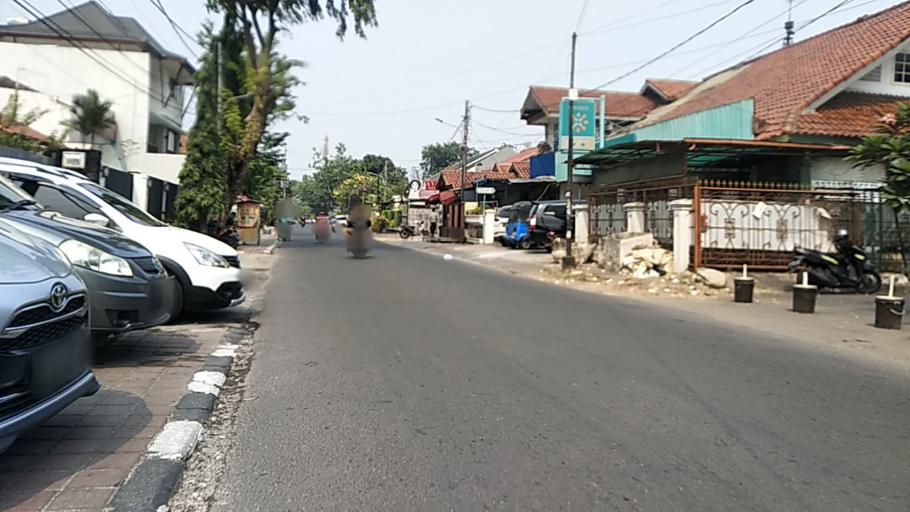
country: ID
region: Jakarta Raya
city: Jakarta
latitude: -6.2305
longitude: 106.8494
